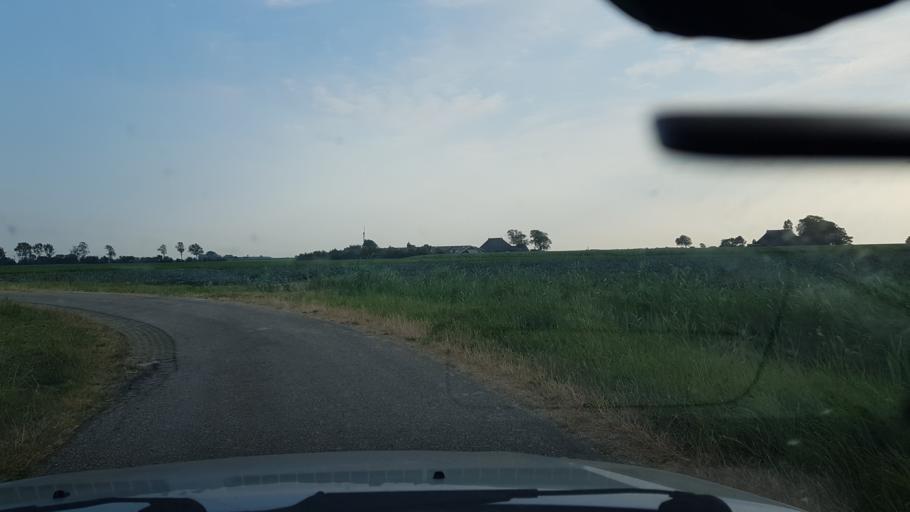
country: NL
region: Friesland
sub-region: Gemeente Ferwerderadiel
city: Ferwert
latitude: 53.3359
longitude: 5.8682
